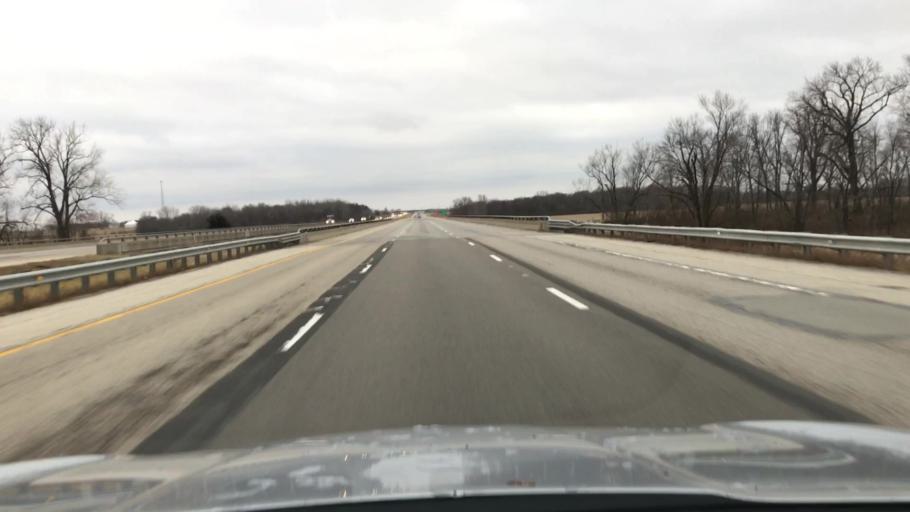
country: US
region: Illinois
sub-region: Logan County
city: Lincoln
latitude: 40.1299
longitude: -89.4171
